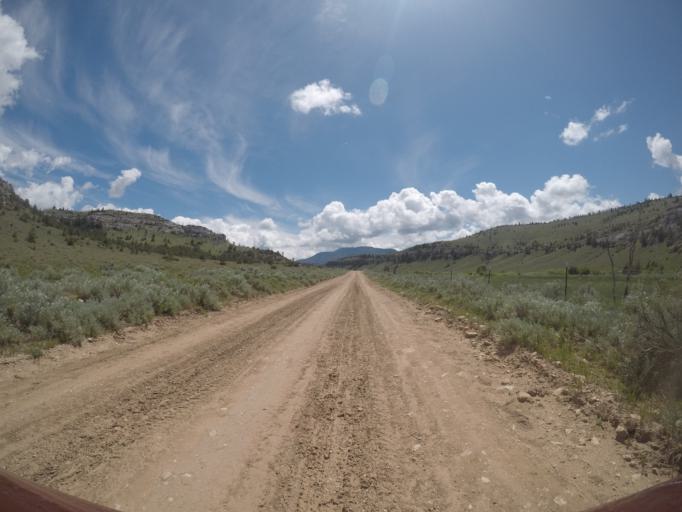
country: US
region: Montana
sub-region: Yellowstone County
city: Laurel
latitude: 45.2368
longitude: -108.6235
